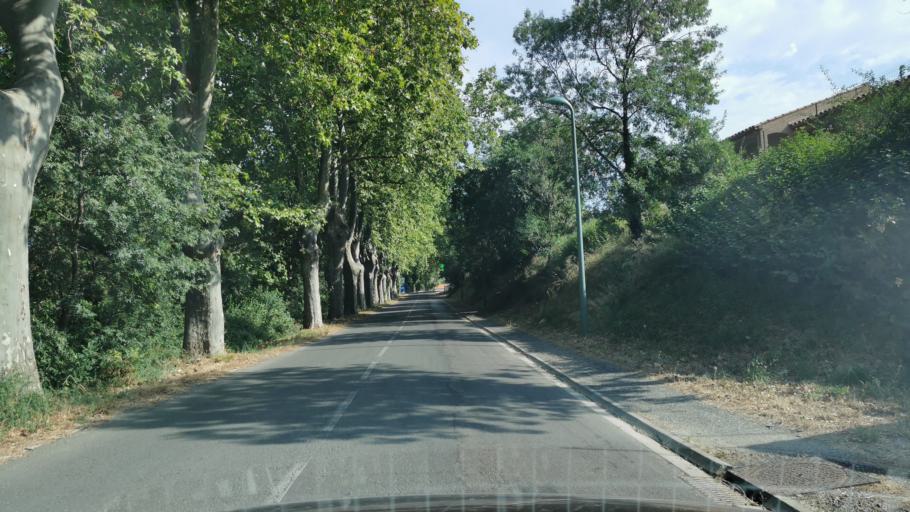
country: FR
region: Languedoc-Roussillon
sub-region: Departement de l'Aude
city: Bize-Minervois
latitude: 43.3112
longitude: 2.8711
